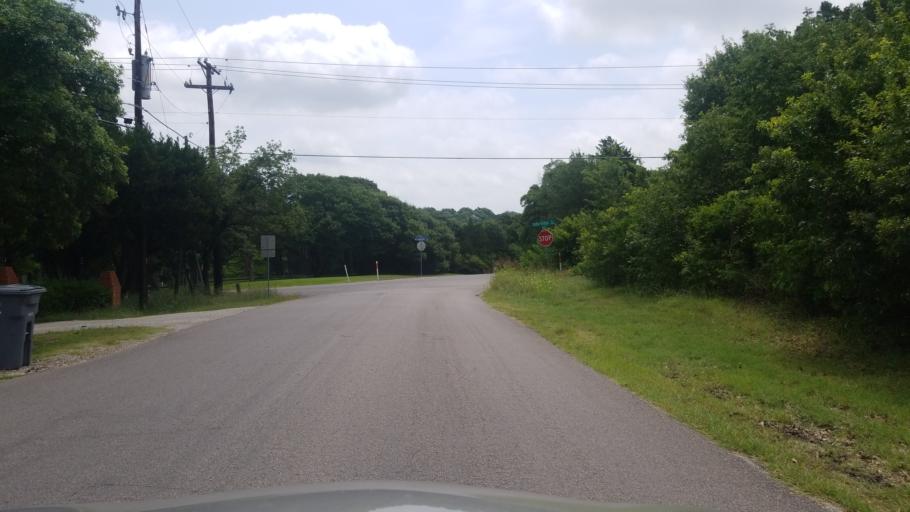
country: US
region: Texas
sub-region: Dallas County
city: Duncanville
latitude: 32.6765
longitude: -96.9263
